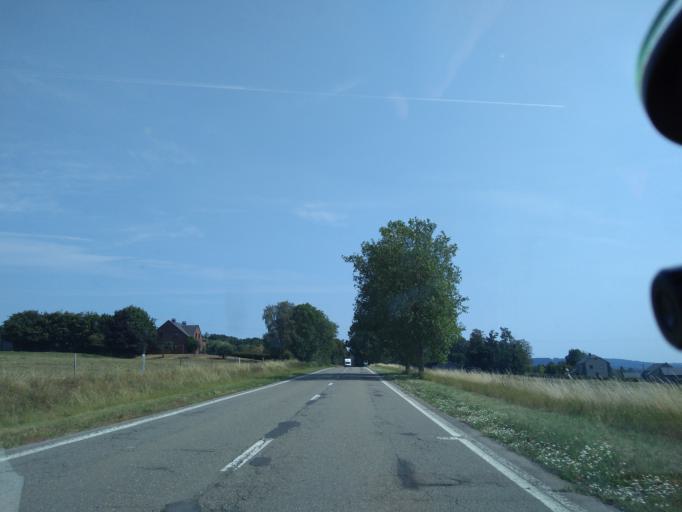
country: BE
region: Wallonia
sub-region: Province du Luxembourg
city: La Roche-en-Ardenne
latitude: 50.1664
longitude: 5.5432
